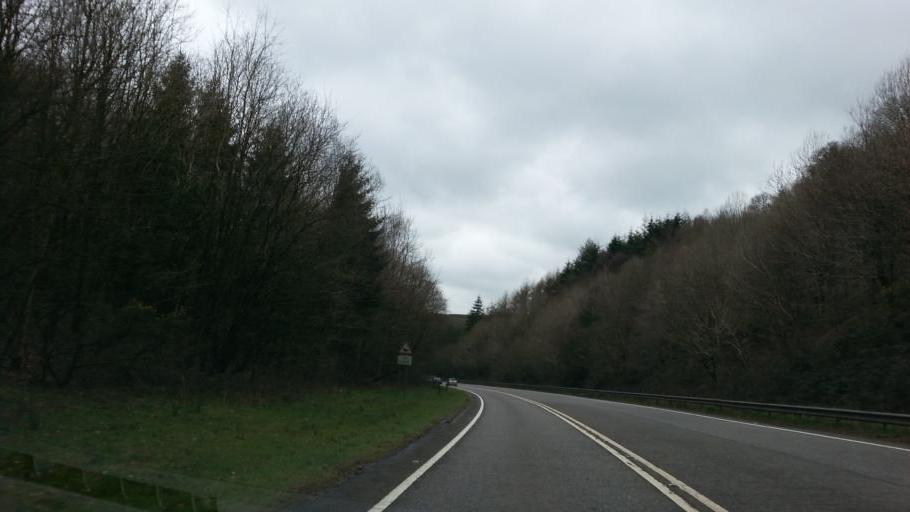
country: GB
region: England
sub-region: Devon
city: South Molton
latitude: 51.0474
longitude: -3.8719
